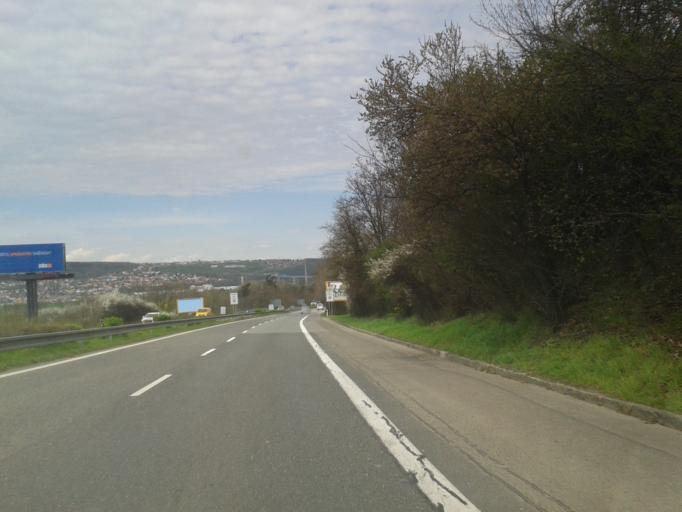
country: CZ
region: Central Bohemia
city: Vrane nad Vltavou
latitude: 49.9671
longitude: 14.3762
